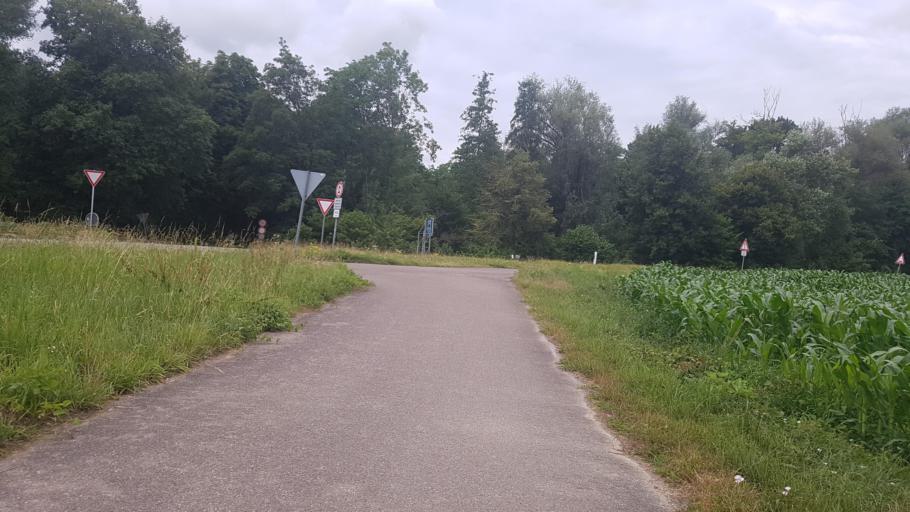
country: DE
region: Baden-Wuerttemberg
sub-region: Karlsruhe Region
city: Steinmauern
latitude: 48.8924
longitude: 8.2145
